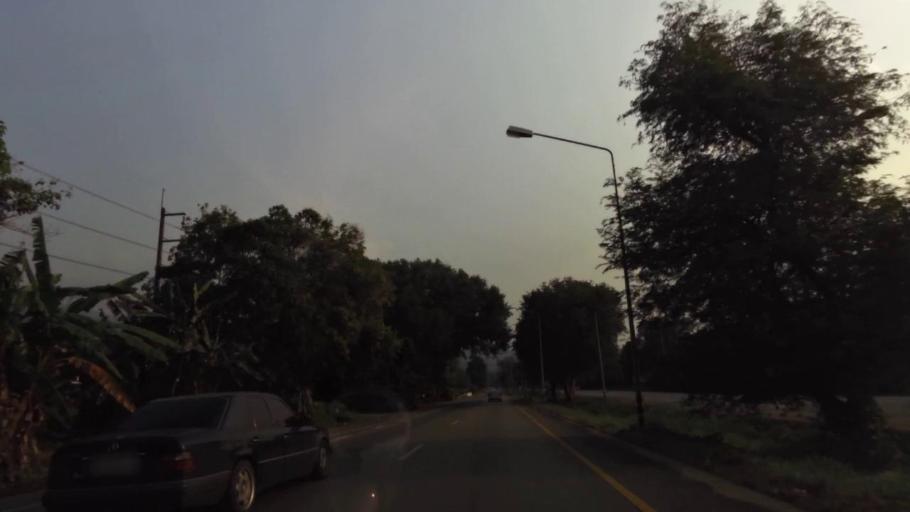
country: TH
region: Chanthaburi
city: Chanthaburi
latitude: 12.5816
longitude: 102.1585
